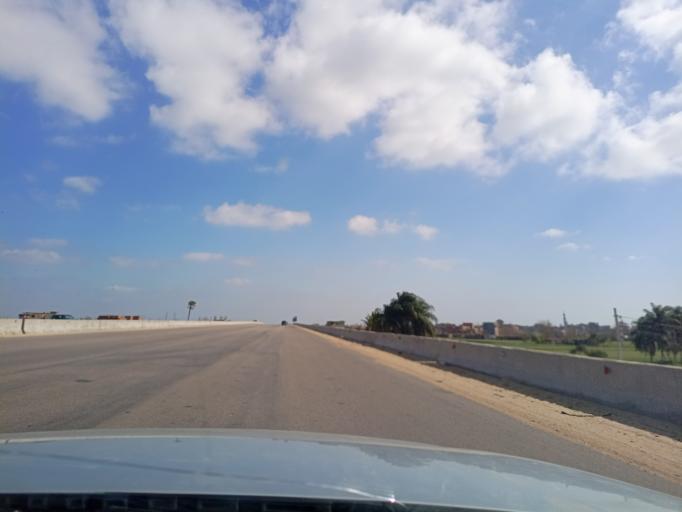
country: EG
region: Muhafazat al Minufiyah
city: Al Bajur
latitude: 30.4003
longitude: 31.0244
